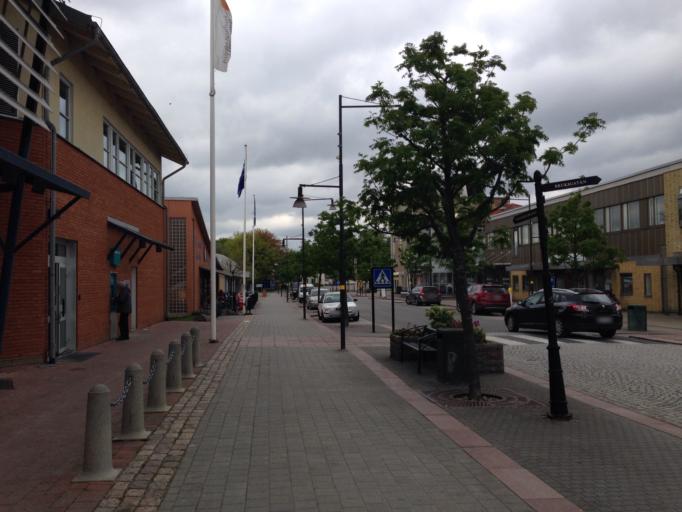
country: SE
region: Skane
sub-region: Bromolla Kommun
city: Bromoella
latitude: 56.0736
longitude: 14.4675
